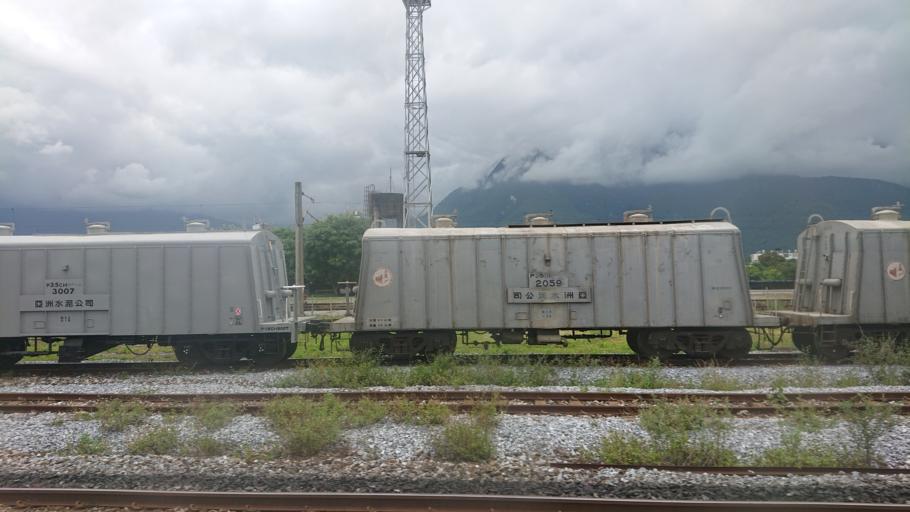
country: TW
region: Taiwan
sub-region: Hualien
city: Hualian
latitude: 23.9979
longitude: 121.6033
